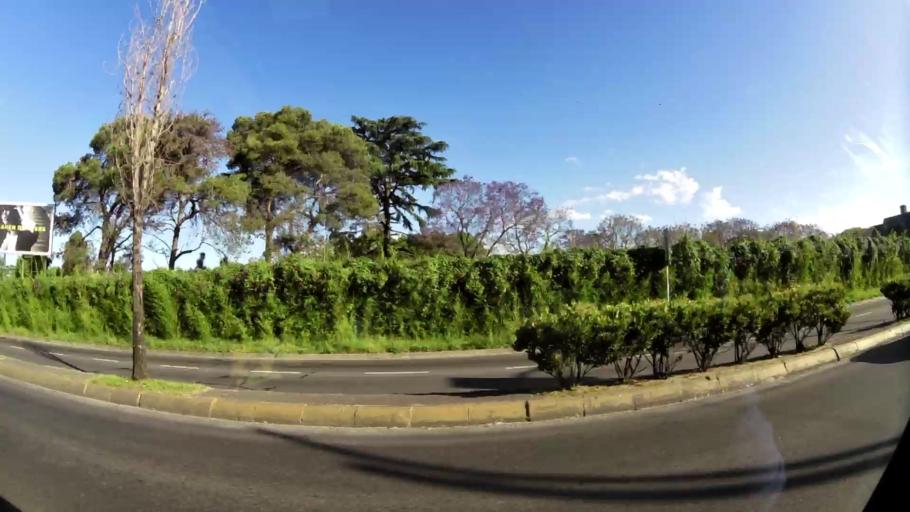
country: AR
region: Buenos Aires
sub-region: Partido de San Isidro
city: San Isidro
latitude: -34.4844
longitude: -58.5319
